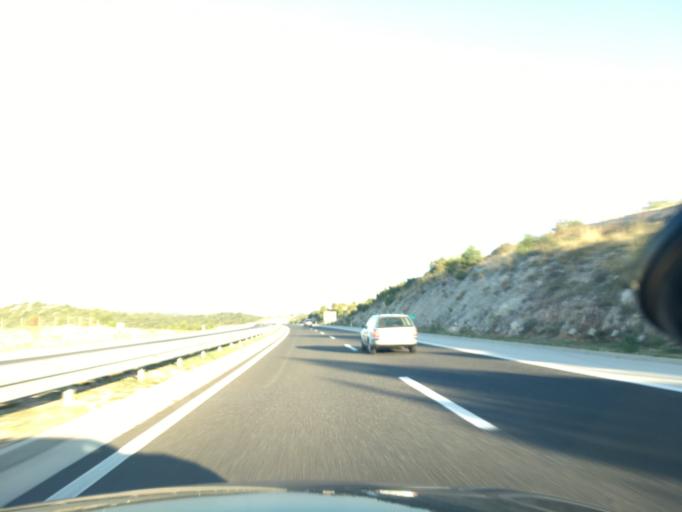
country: HR
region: Sibensko-Kniniska
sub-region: Grad Sibenik
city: Sibenik
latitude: 43.7508
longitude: 15.9518
